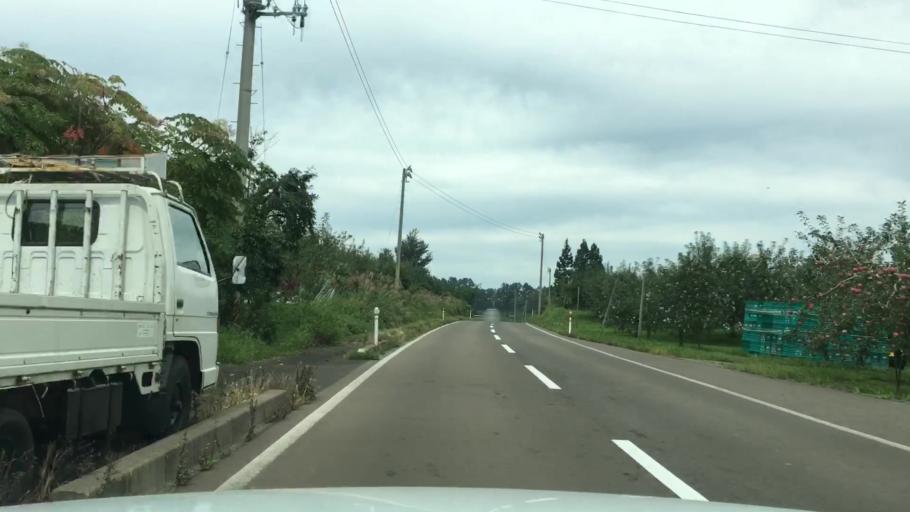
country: JP
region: Aomori
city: Hirosaki
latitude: 40.6723
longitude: 140.3857
